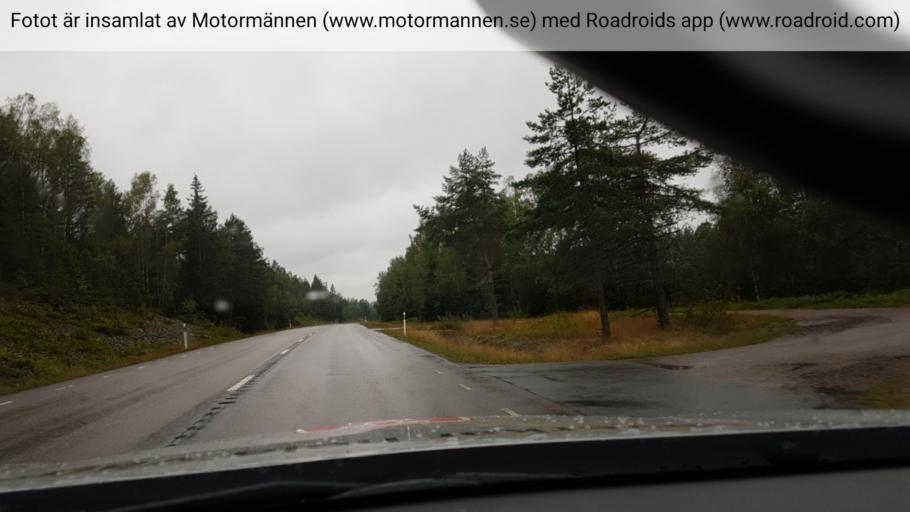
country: SE
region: Vaestra Goetaland
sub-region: Bengtsfors Kommun
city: Billingsfors
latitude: 58.9323
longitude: 12.1773
